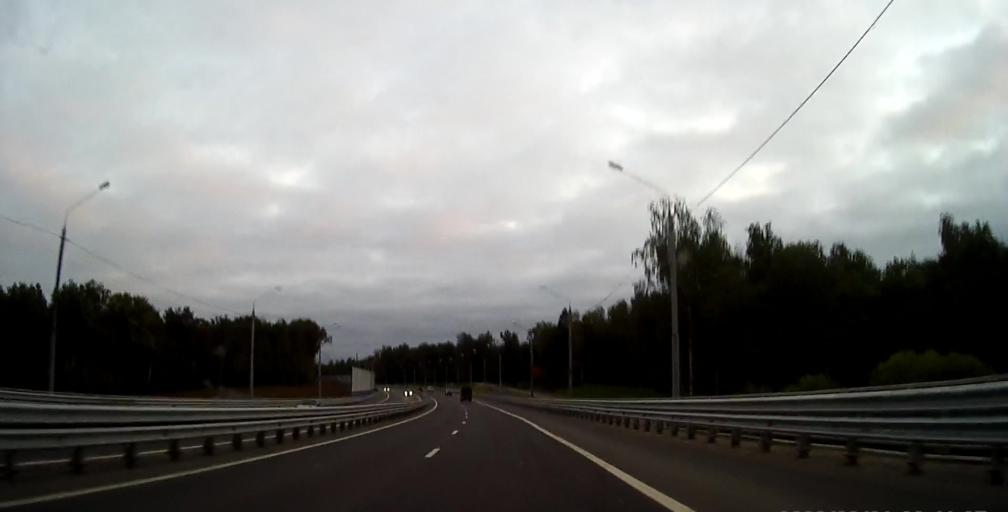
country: RU
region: Moskovskaya
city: Dubrovitsy
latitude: 55.4062
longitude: 37.5016
